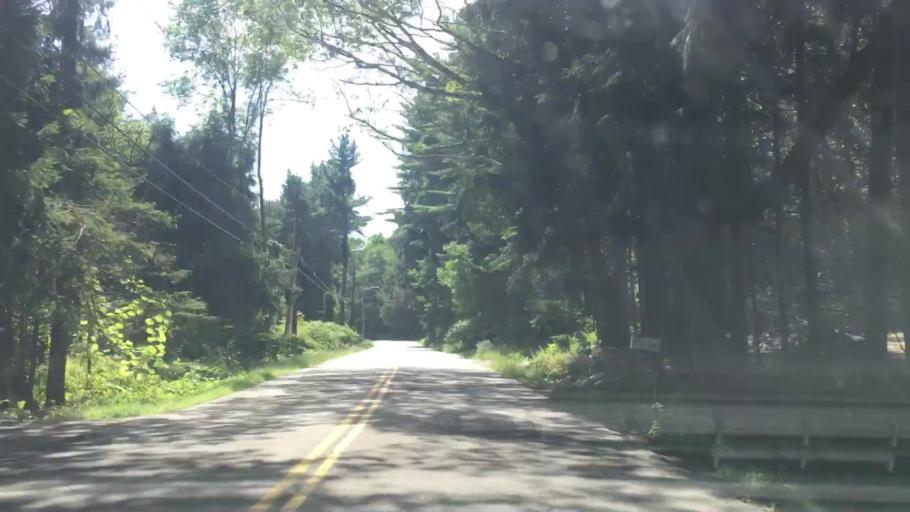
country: US
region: Maine
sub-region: Cumberland County
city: South Portland
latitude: 43.6113
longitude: -70.2646
